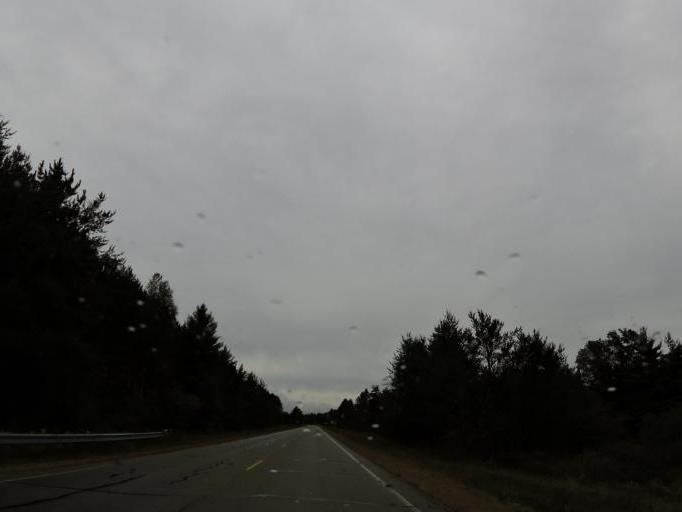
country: US
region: Michigan
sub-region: Roscommon County
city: Roscommon
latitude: 44.4546
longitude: -84.5241
